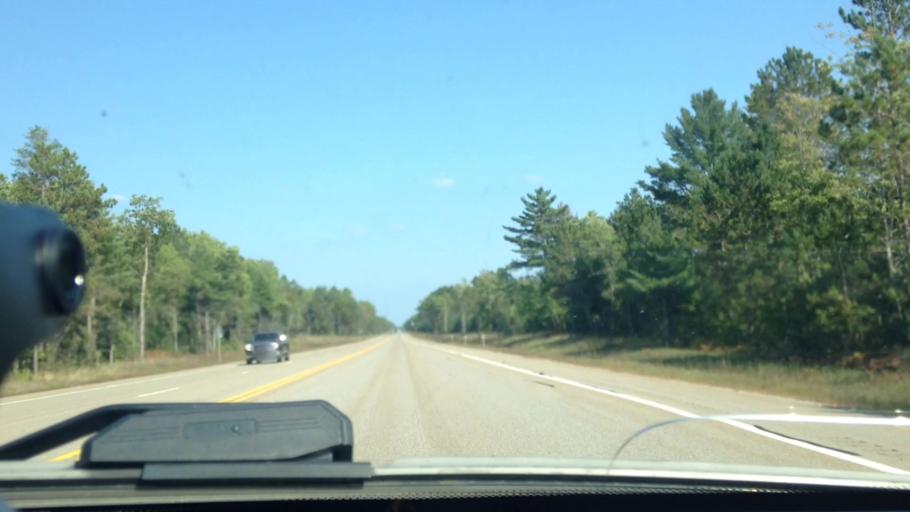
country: US
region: Michigan
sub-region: Chippewa County
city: Sault Ste. Marie
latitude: 46.3654
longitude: -84.7593
